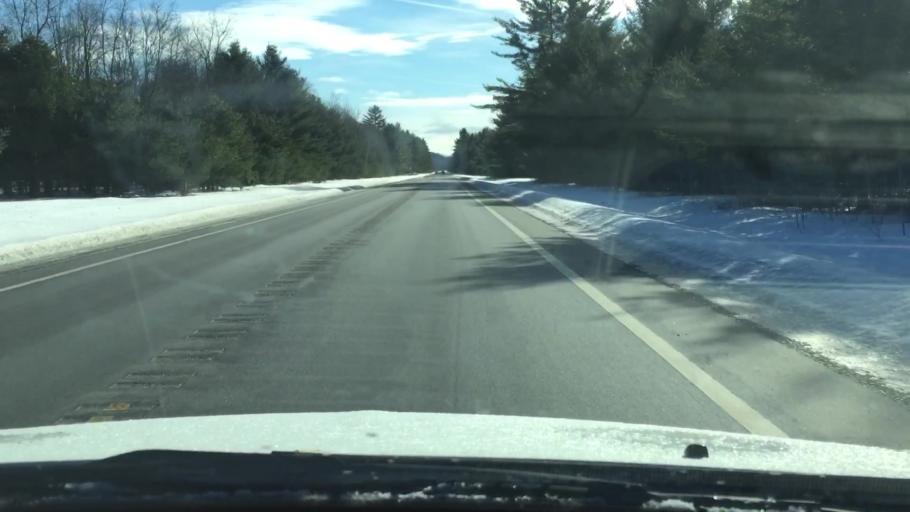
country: US
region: Michigan
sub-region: Charlevoix County
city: East Jordan
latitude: 45.0371
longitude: -85.0679
